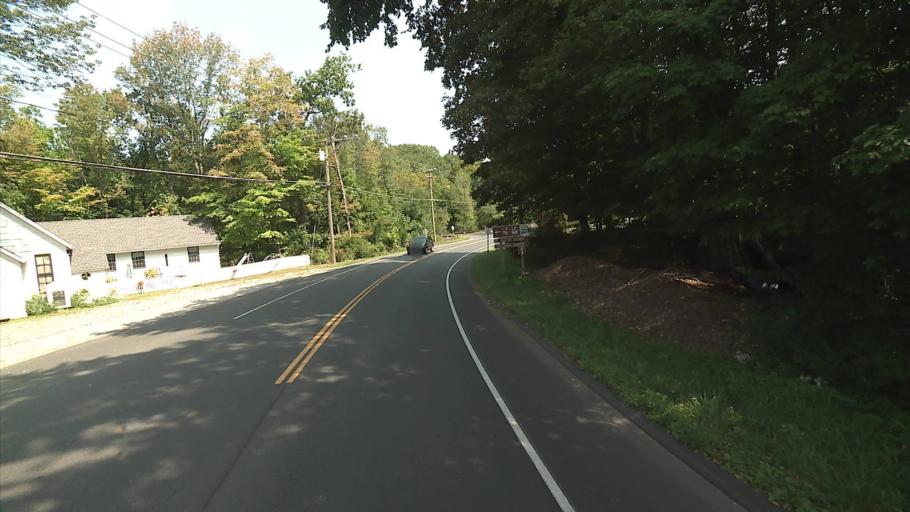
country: US
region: Connecticut
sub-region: Fairfield County
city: Bethel
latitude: 41.3812
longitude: -73.3742
